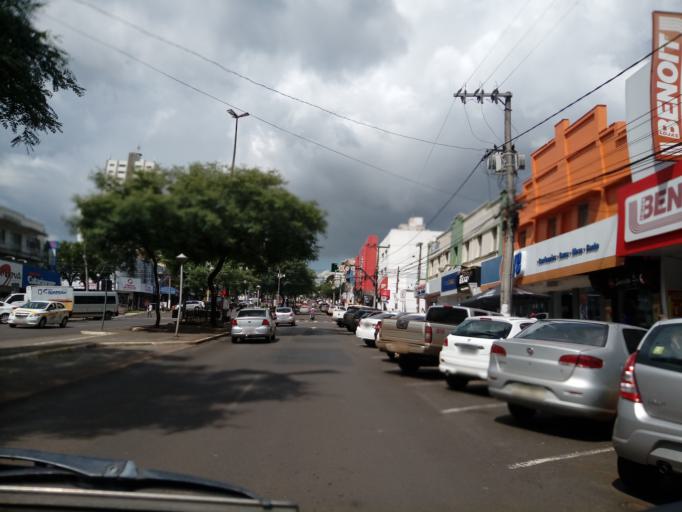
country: BR
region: Santa Catarina
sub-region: Chapeco
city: Chapeco
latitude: -27.1011
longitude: -52.6154
